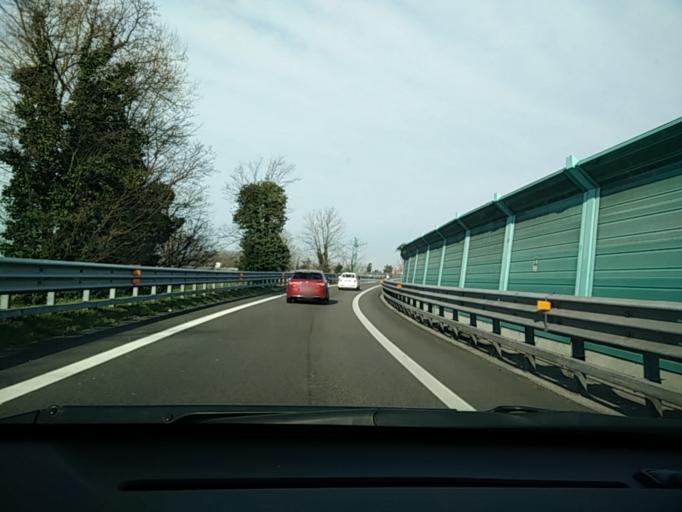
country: IT
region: Veneto
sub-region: Provincia di Padova
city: Noventa
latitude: 45.4196
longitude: 11.9426
